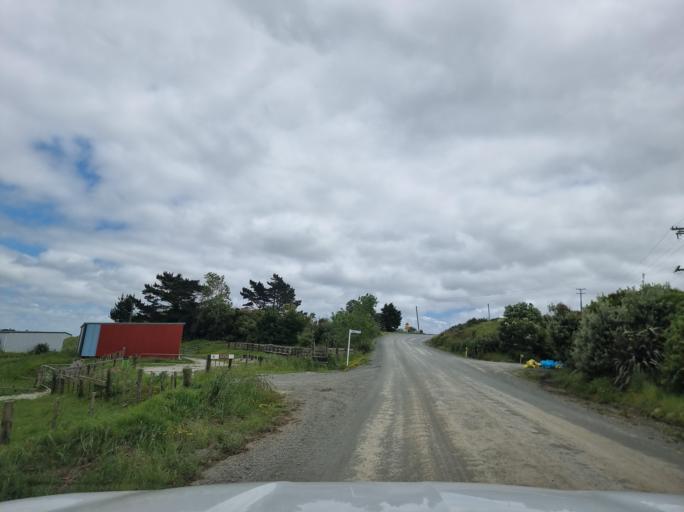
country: NZ
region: Auckland
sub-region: Auckland
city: Wellsford
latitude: -36.1379
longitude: 174.5364
